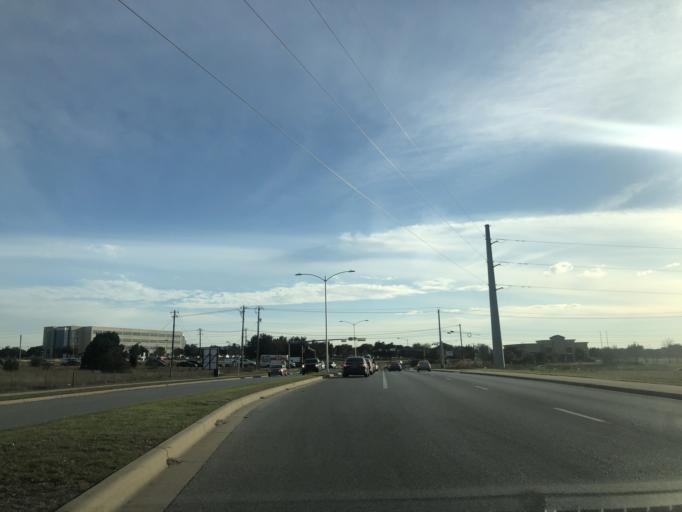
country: US
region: Texas
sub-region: Travis County
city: Wells Branch
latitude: 30.4066
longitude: -97.6637
